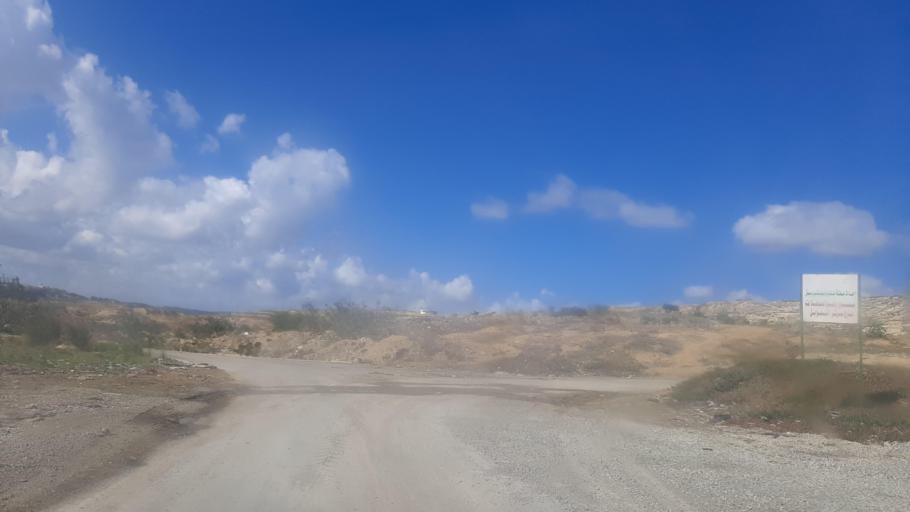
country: TN
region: Nabul
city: Nabeul
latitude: 36.4928
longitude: 10.7057
